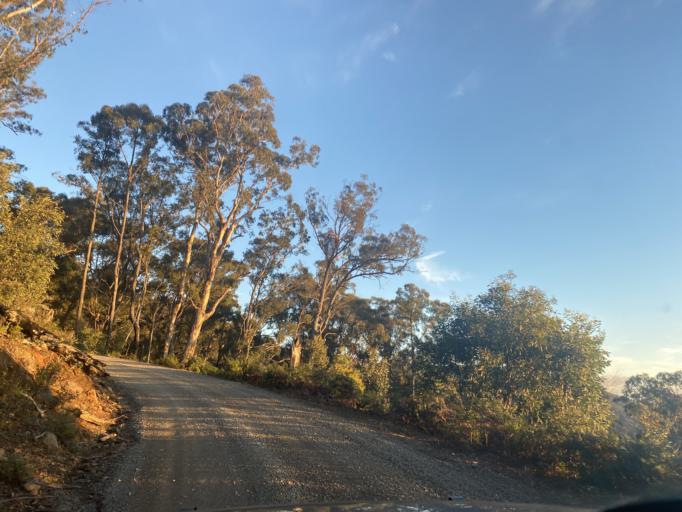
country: AU
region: Victoria
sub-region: Yarra Ranges
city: Healesville
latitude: -37.4292
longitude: 145.5291
